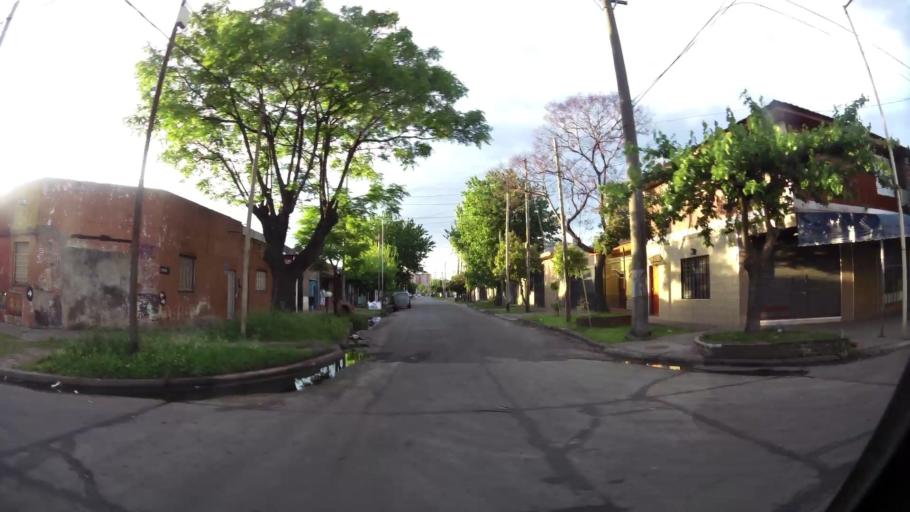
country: AR
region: Buenos Aires
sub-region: Partido de Avellaneda
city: Avellaneda
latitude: -34.7076
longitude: -58.3390
